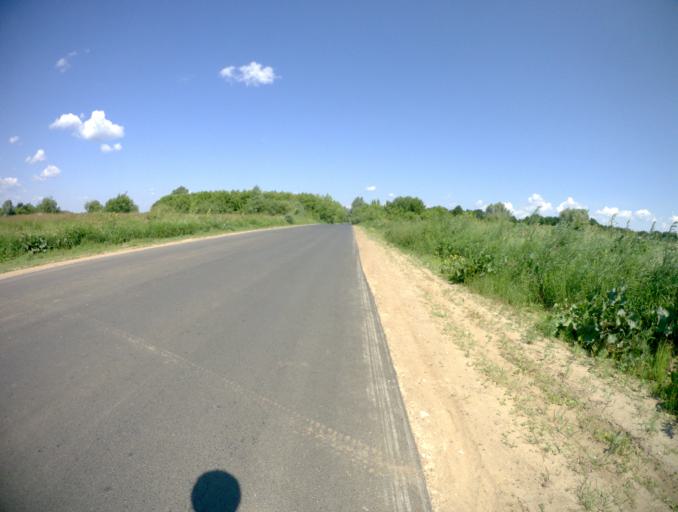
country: RU
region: Vladimir
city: Vyazniki
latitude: 56.2582
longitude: 42.1736
